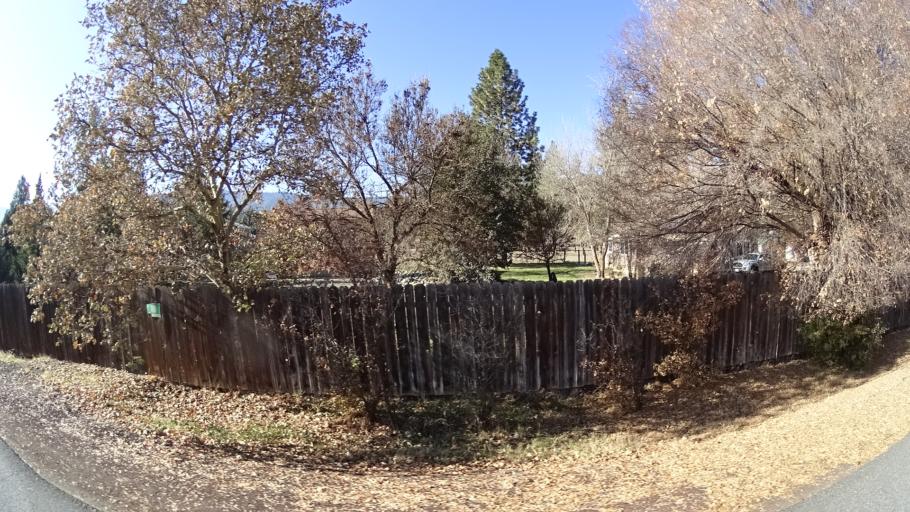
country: US
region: California
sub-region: Siskiyou County
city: Yreka
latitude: 41.6841
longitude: -122.6368
